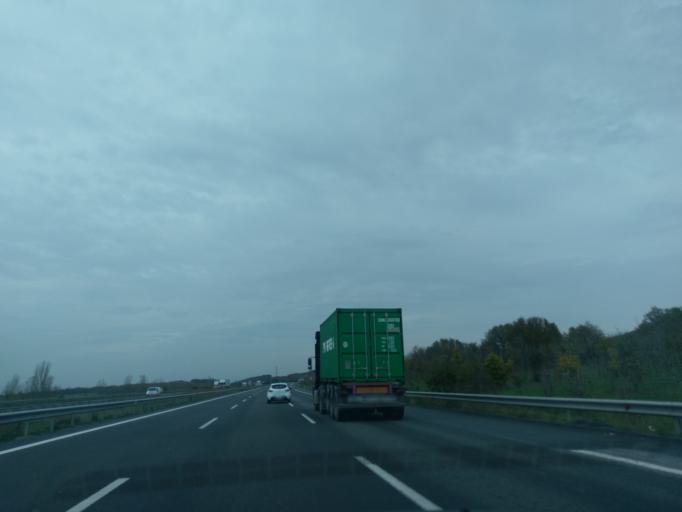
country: TR
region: Istanbul
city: Canta
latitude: 41.1757
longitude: 28.1165
